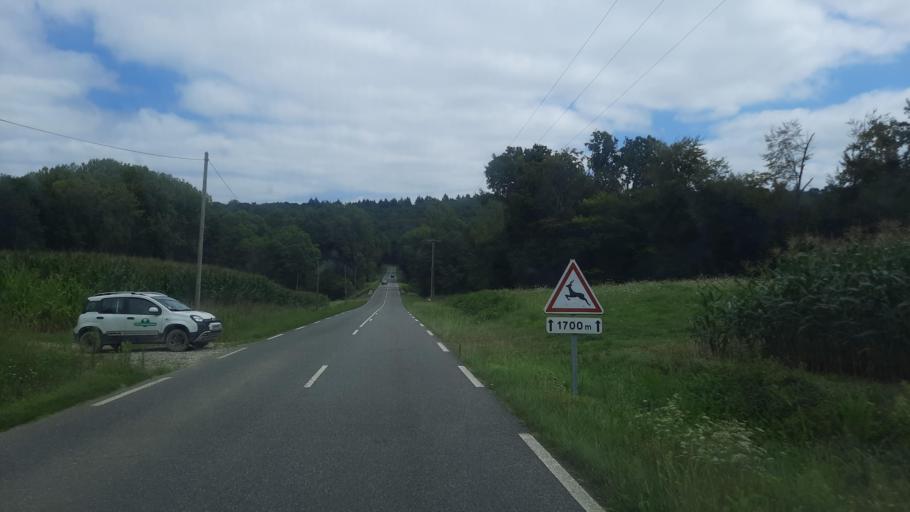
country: FR
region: Midi-Pyrenees
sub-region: Departement des Hautes-Pyrenees
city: Trie-sur-Baise
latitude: 43.2989
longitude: 0.4257
